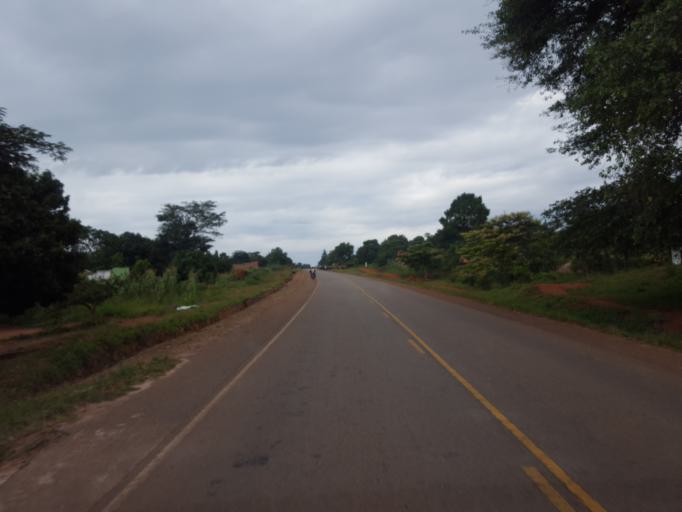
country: UG
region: Central Region
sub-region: Kiboga District
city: Kiboga
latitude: 1.0157
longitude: 31.6904
